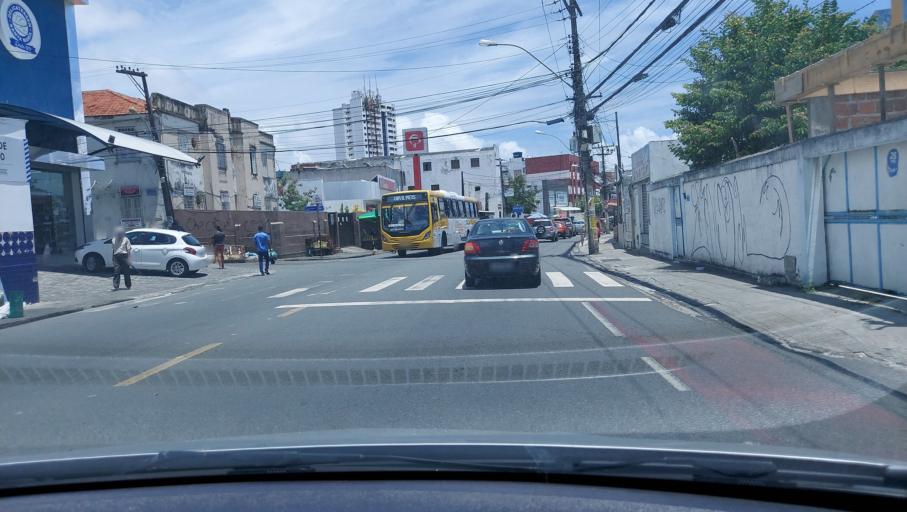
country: BR
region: Bahia
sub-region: Salvador
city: Salvador
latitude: -12.9888
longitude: -38.4818
